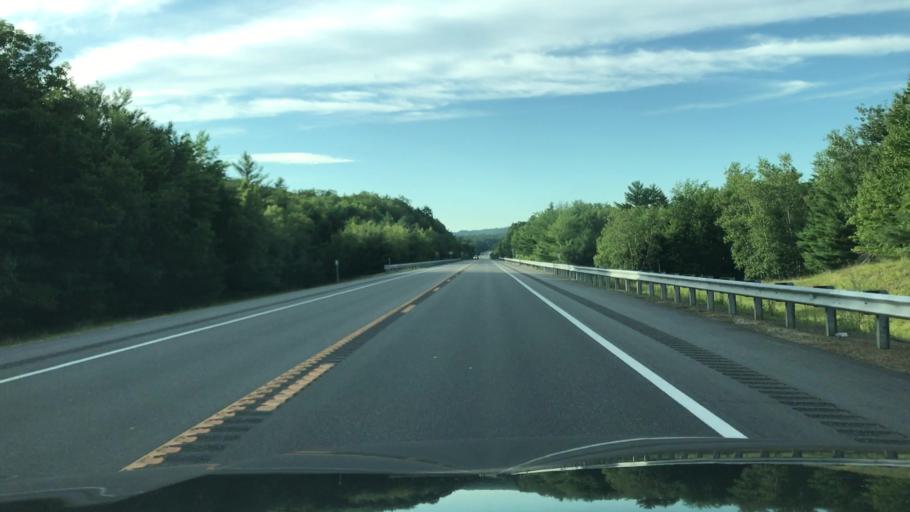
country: US
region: New Hampshire
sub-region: Strafford County
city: Farmington
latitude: 43.3888
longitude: -70.9995
